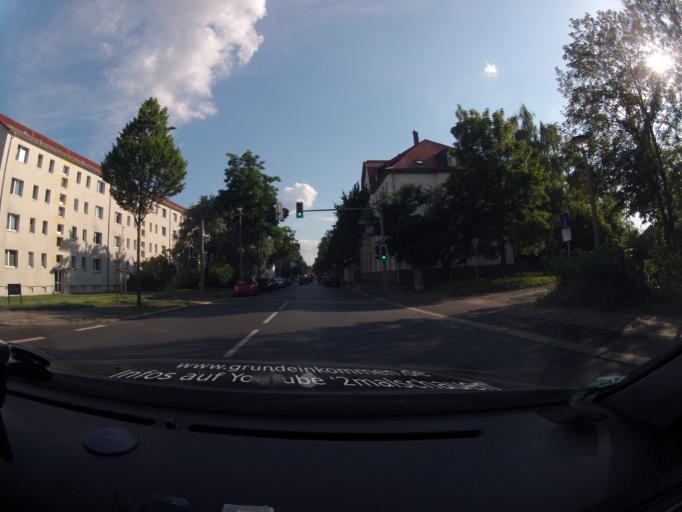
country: DE
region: Saxony
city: Leipzig
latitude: 51.3183
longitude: 12.4196
